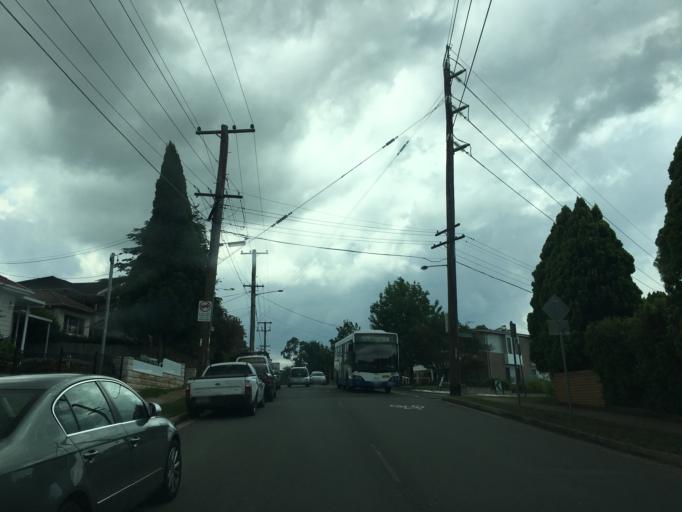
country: AU
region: New South Wales
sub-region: Ryde
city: Denistone
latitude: -33.7947
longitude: 151.1022
